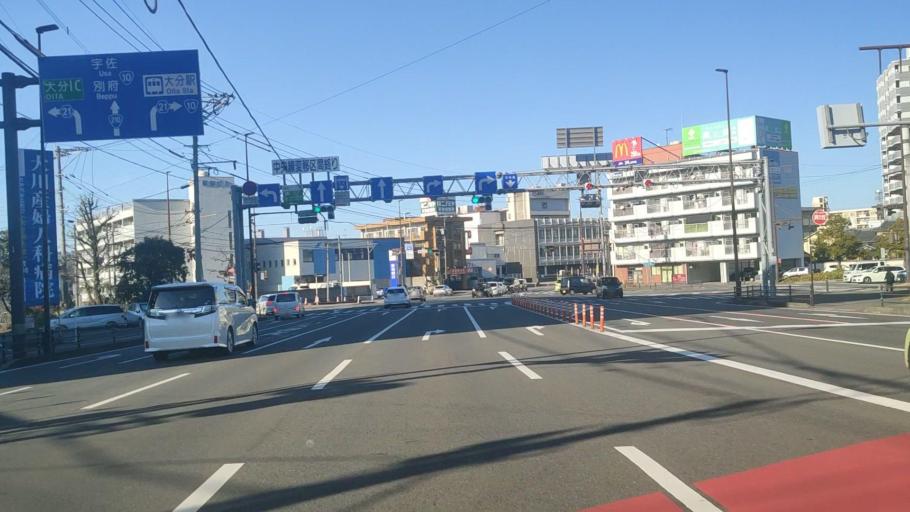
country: JP
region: Oita
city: Oita
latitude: 33.2253
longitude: 131.5955
